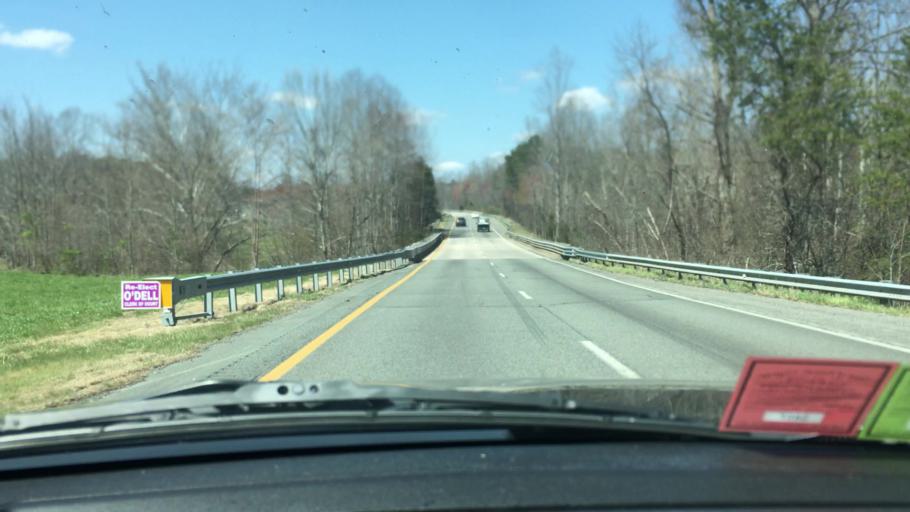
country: US
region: North Carolina
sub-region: Surry County
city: Pilot Mountain
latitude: 36.3965
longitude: -80.4915
